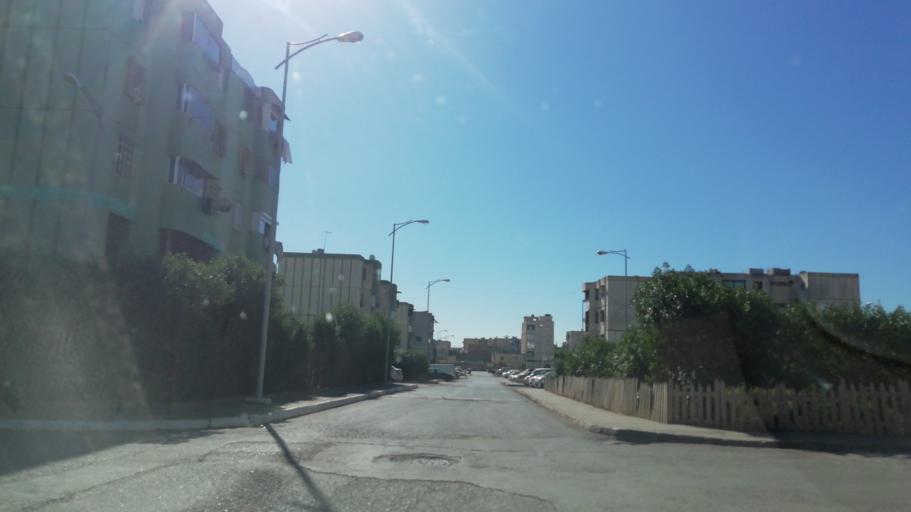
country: DZ
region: Oran
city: Oran
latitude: 35.6887
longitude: -0.6107
